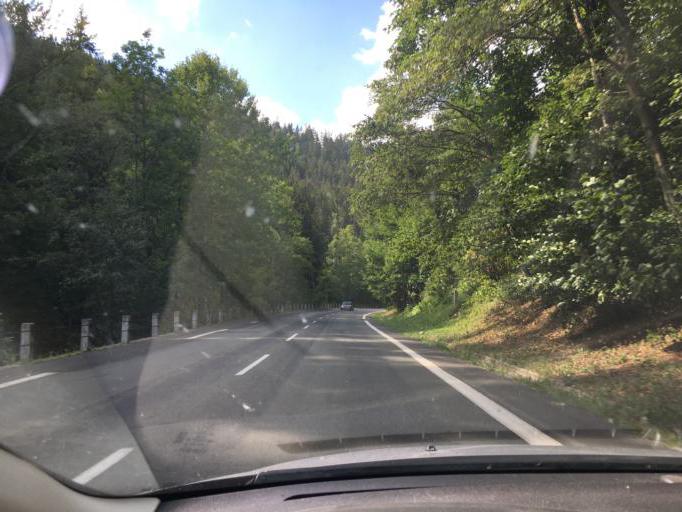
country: CZ
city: Benecko
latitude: 50.6731
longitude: 15.5940
